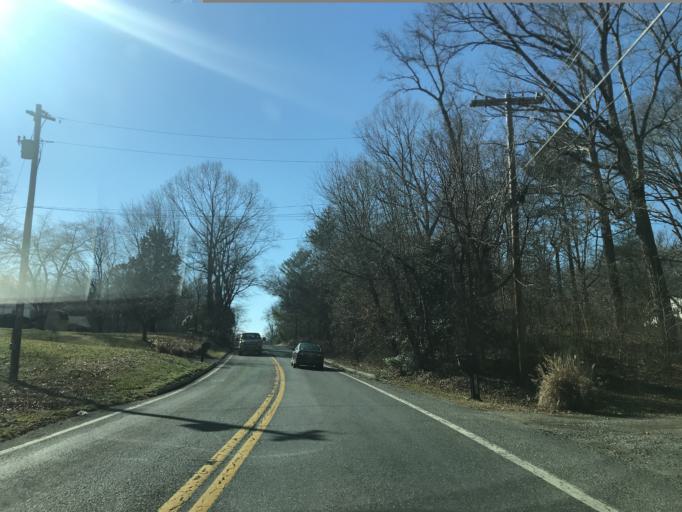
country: US
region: Maryland
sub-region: Charles County
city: Bennsville
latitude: 38.5887
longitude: -77.0079
